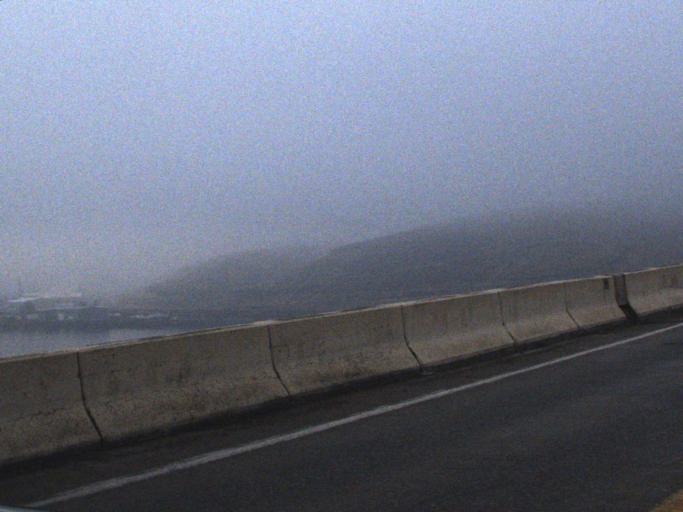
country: US
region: Washington
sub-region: Asotin County
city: West Clarkston-Highland
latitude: 46.4234
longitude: -117.0708
